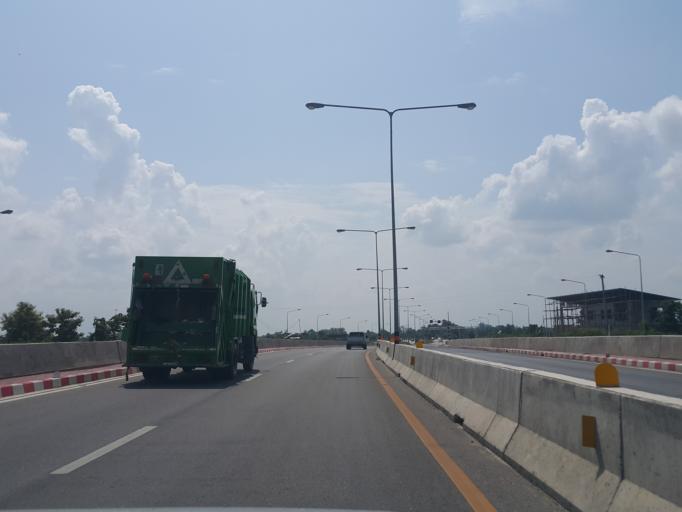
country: TH
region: Chiang Mai
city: Mae Wang
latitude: 18.6028
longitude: 98.8347
